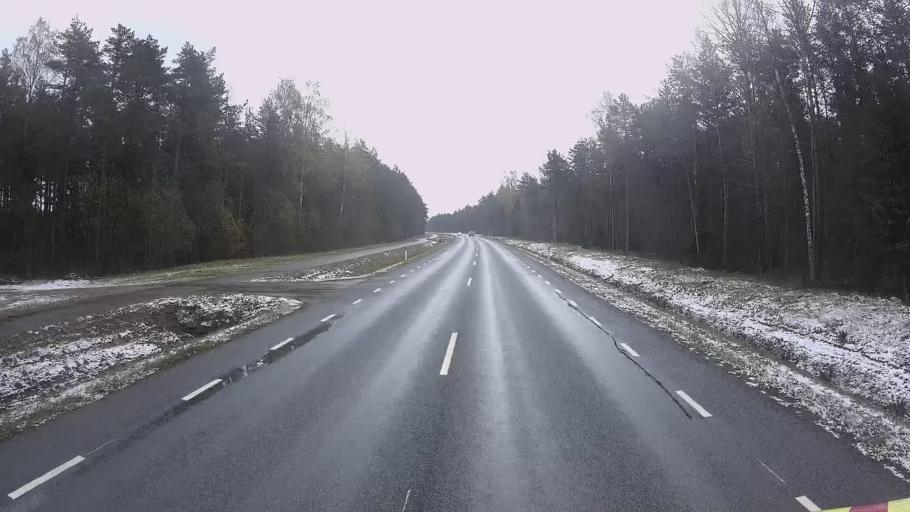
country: EE
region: Hiiumaa
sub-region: Kaerdla linn
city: Kardla
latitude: 58.9987
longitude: 22.7051
